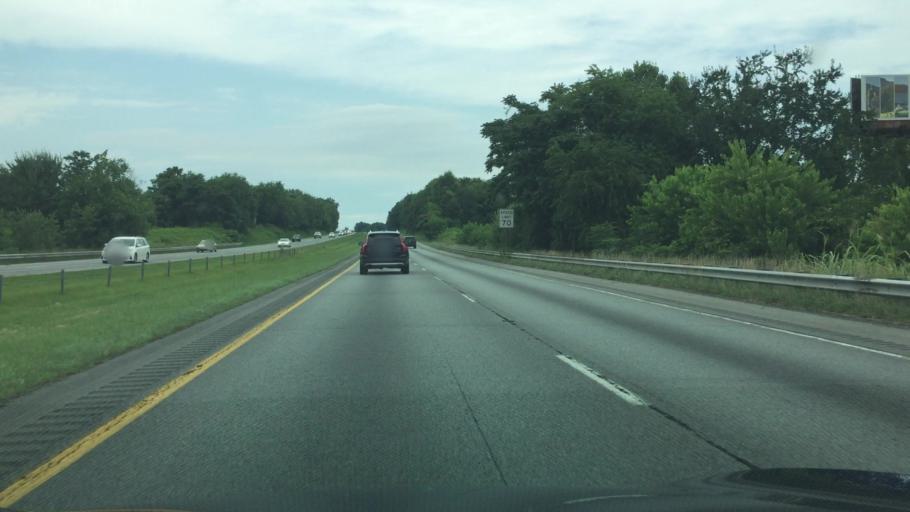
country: US
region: North Carolina
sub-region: Yadkin County
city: Jonesville
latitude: 36.2026
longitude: -80.8110
